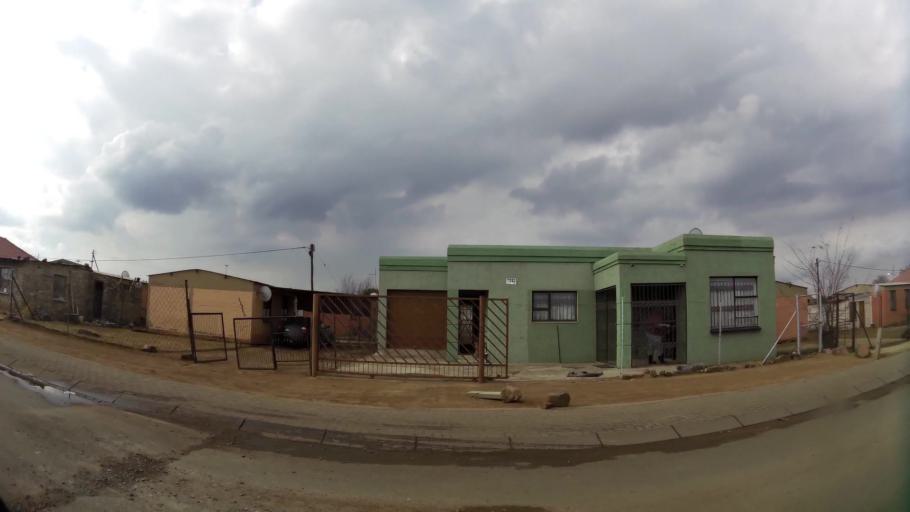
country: ZA
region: Gauteng
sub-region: Sedibeng District Municipality
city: Vanderbijlpark
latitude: -26.7007
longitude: 27.8028
